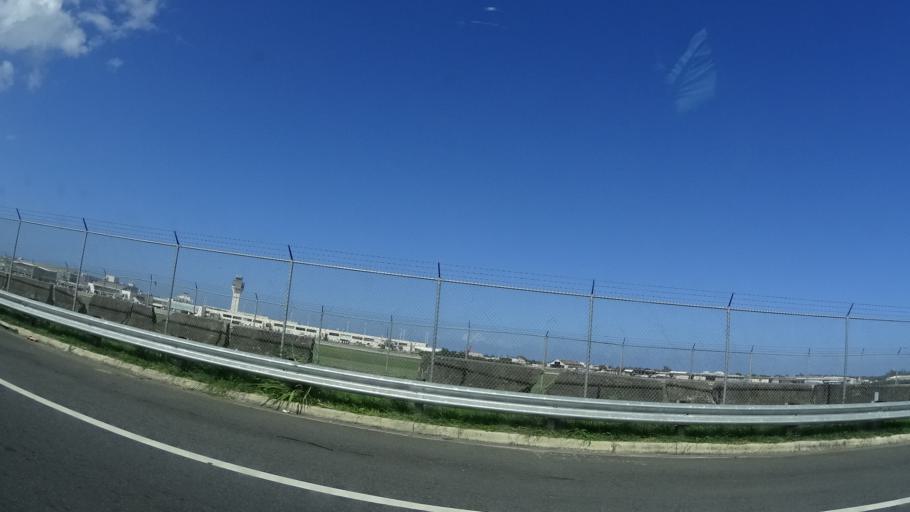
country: PR
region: Carolina
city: Carolina
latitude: 18.4319
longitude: -66.0006
